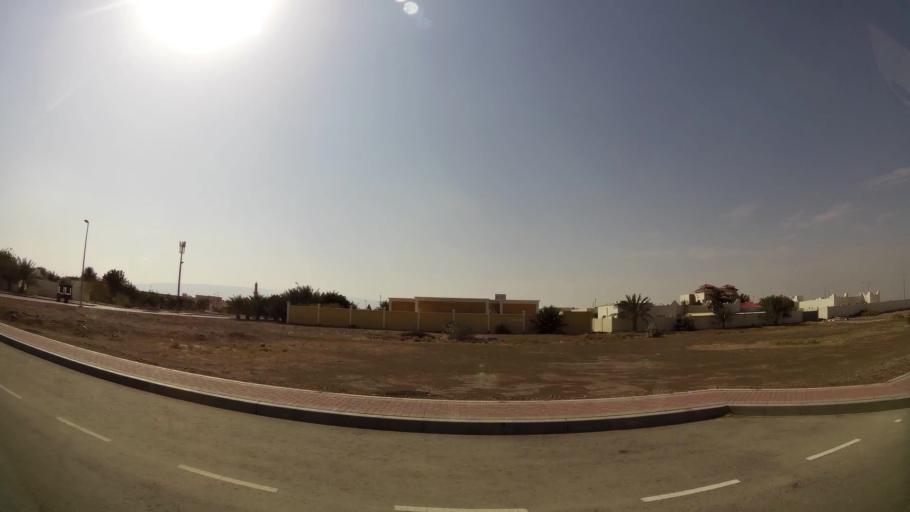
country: AE
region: Abu Dhabi
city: Al Ain
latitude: 24.0916
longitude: 55.9357
